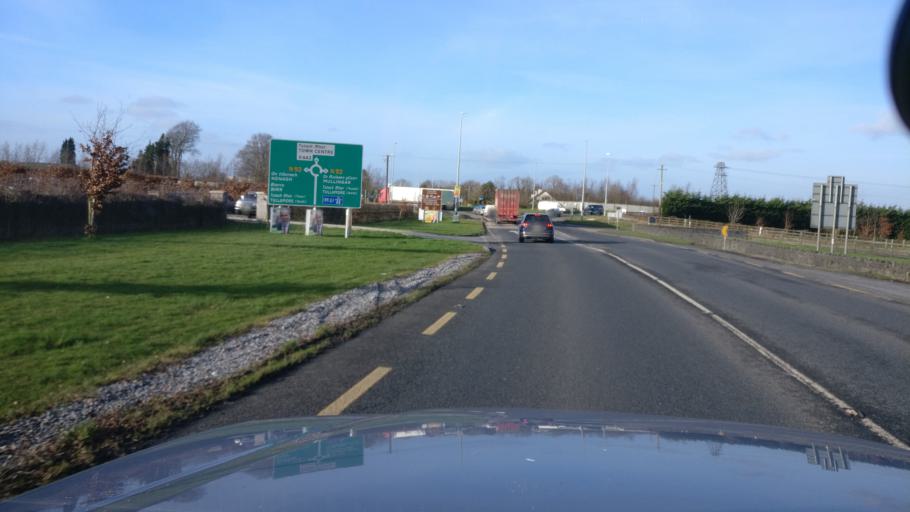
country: IE
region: Leinster
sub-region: Uibh Fhaili
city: Tullamore
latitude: 53.2529
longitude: -7.4775
